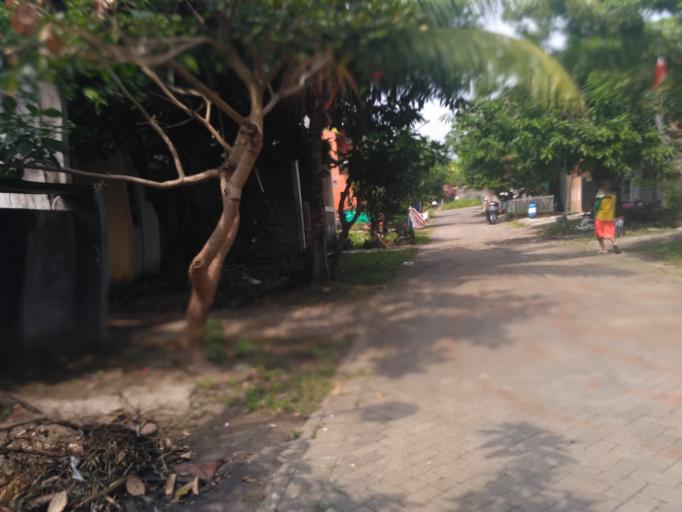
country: ID
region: Central Java
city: Mranggen
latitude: -7.0650
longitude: 110.4573
